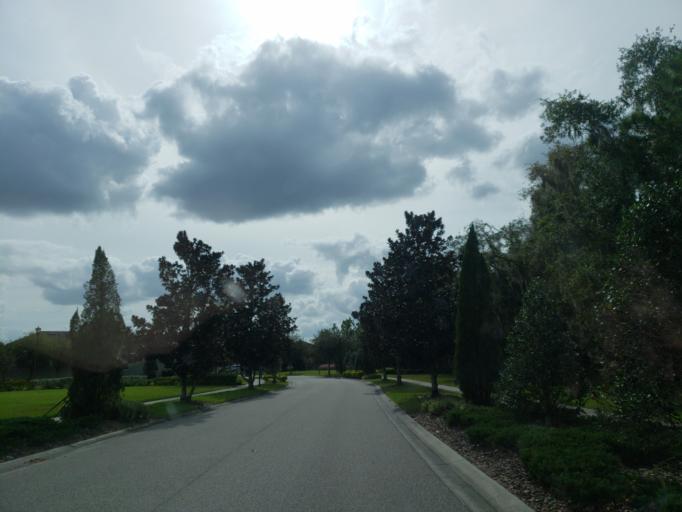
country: US
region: Florida
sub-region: Hillsborough County
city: Fish Hawk
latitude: 27.8401
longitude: -82.2064
